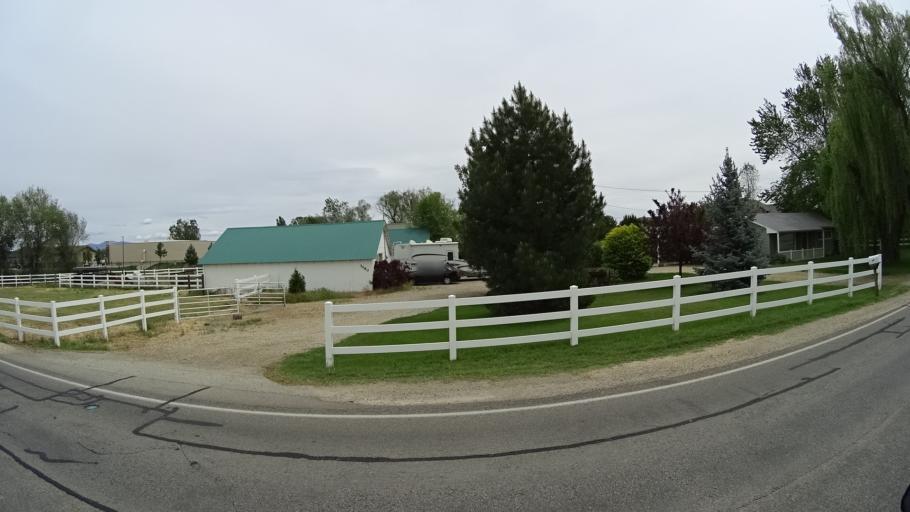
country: US
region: Idaho
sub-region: Ada County
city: Meridian
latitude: 43.5725
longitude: -116.3747
